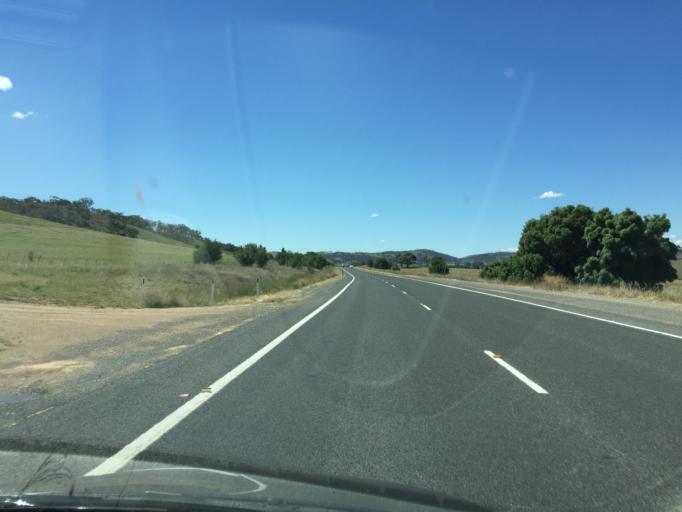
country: AU
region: Australian Capital Territory
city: Macarthur
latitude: -35.7310
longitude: 149.1606
